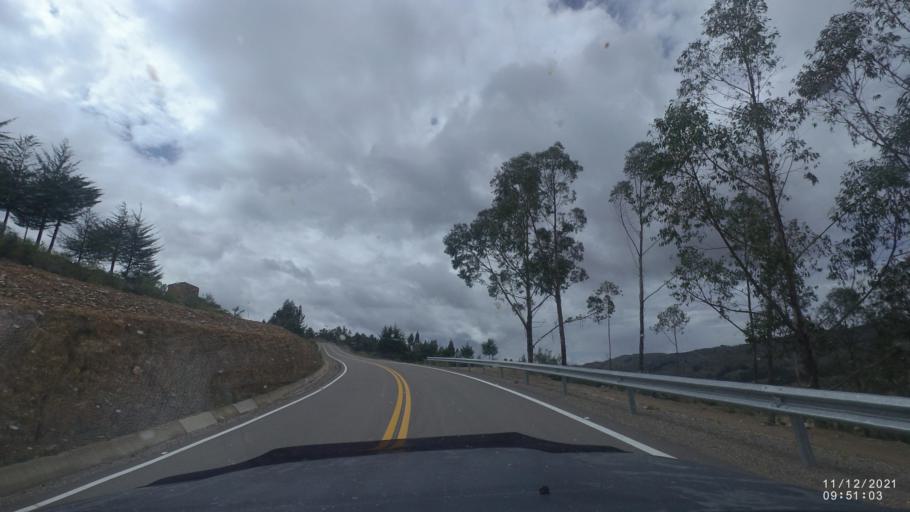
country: BO
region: Cochabamba
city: Tarata
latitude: -17.7877
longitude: -65.9577
